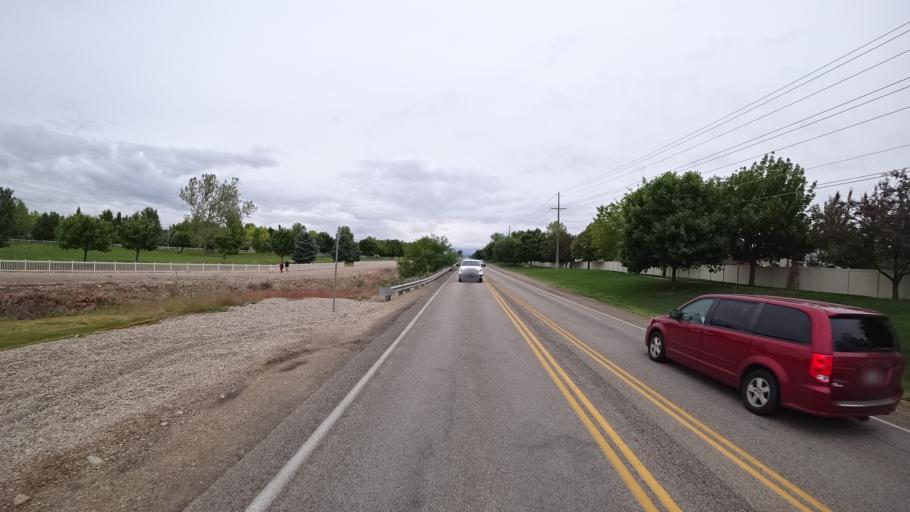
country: US
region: Idaho
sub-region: Ada County
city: Meridian
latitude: 43.6340
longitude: -116.4231
